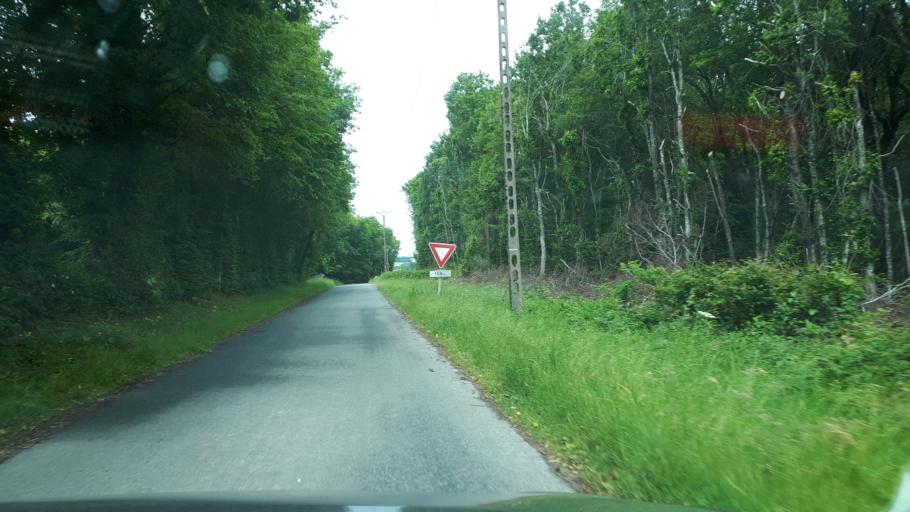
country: FR
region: Centre
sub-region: Departement du Cher
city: Blancafort
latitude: 47.4215
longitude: 2.6095
